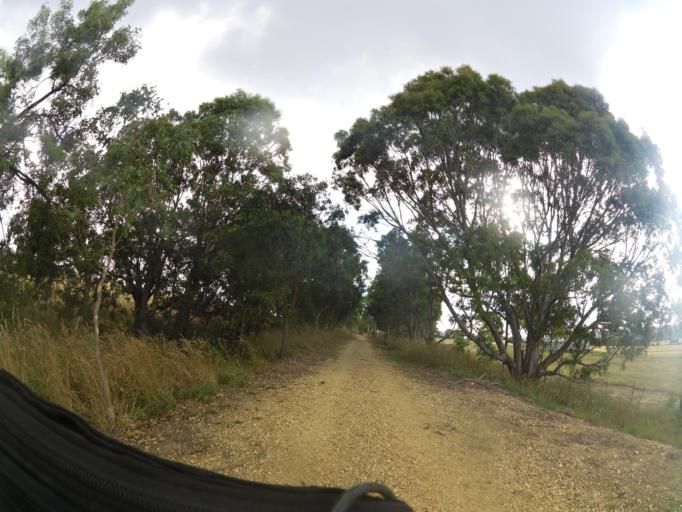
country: AU
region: Victoria
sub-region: Wellington
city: Heyfield
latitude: -38.0234
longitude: 146.6744
